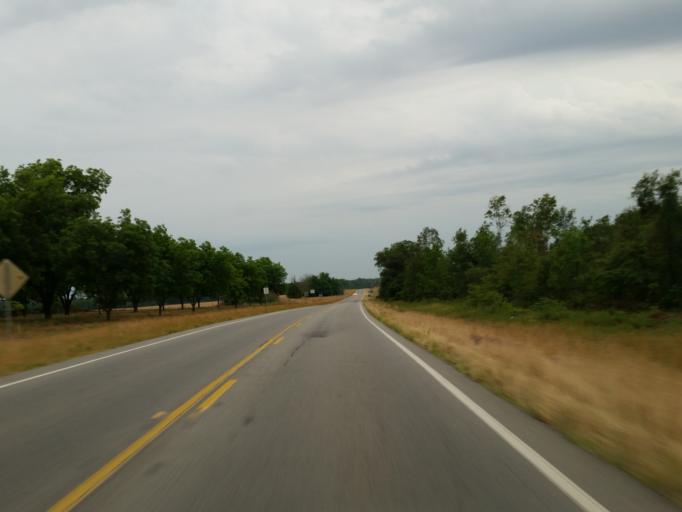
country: US
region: Georgia
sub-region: Dooly County
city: Vienna
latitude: 32.0313
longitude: -83.7922
